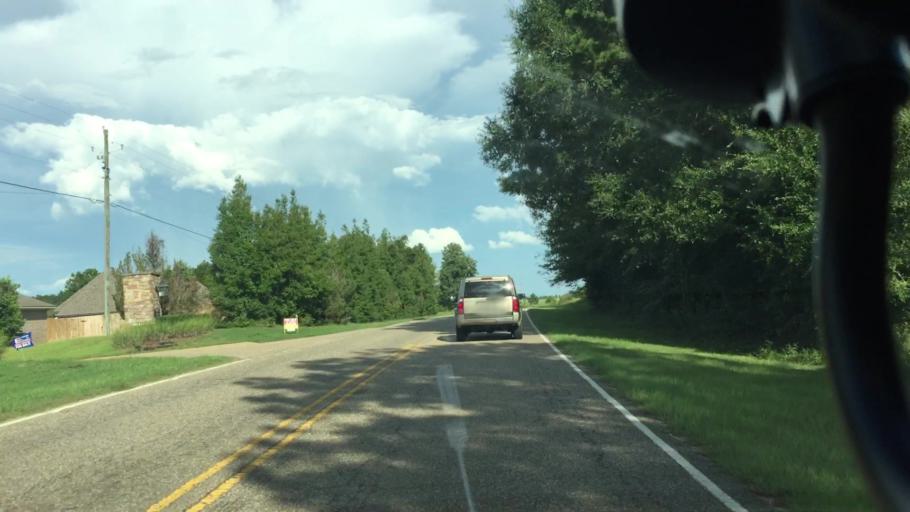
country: US
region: Alabama
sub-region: Coffee County
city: Enterprise
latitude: 31.3701
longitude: -85.8347
